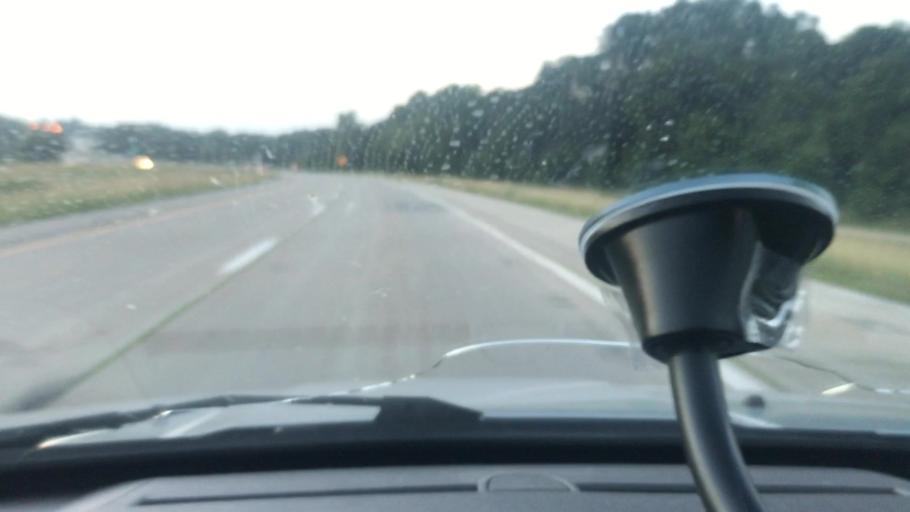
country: US
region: Illinois
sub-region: Peoria County
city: Bellevue
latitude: 40.7442
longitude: -89.6673
